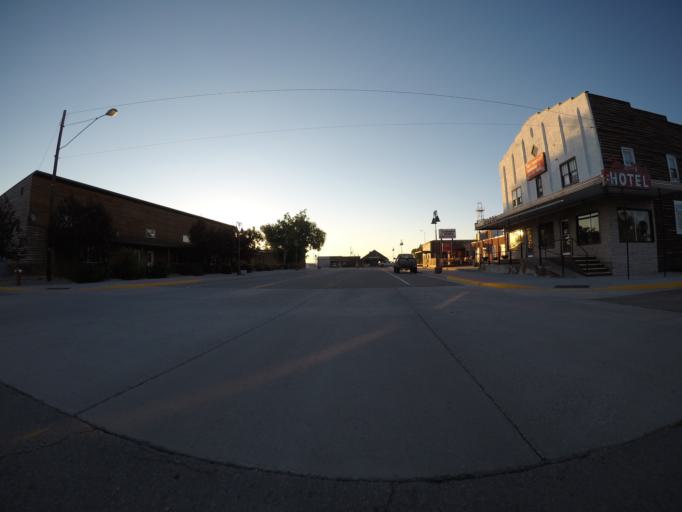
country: US
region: Wyoming
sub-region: Sublette County
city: Marbleton
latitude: 42.5381
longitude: -110.1112
